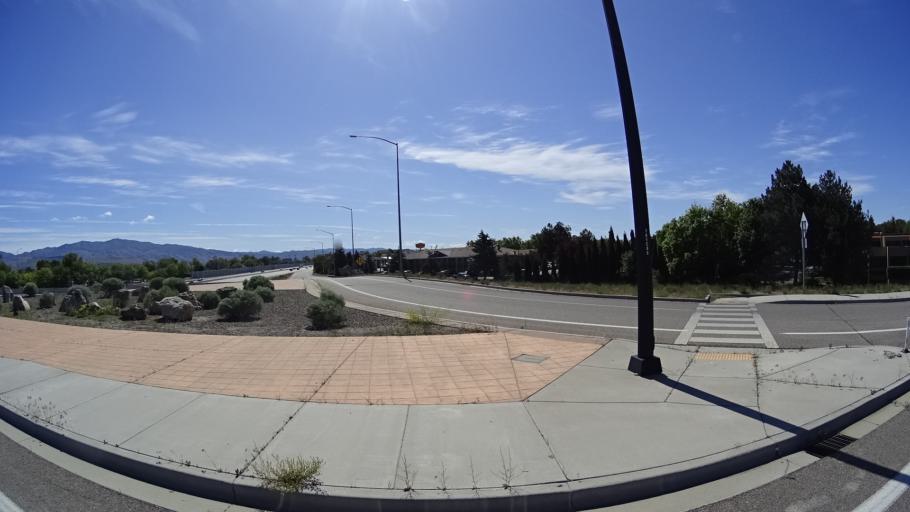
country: US
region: Idaho
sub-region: Ada County
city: Boise
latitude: 43.5705
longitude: -116.2158
